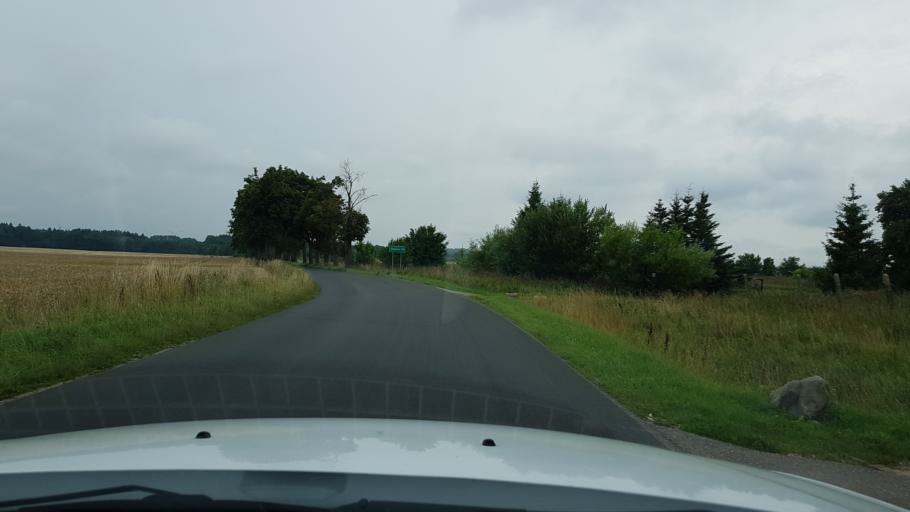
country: PL
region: West Pomeranian Voivodeship
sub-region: Powiat slawienski
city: Slawno
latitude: 54.5046
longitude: 16.5734
